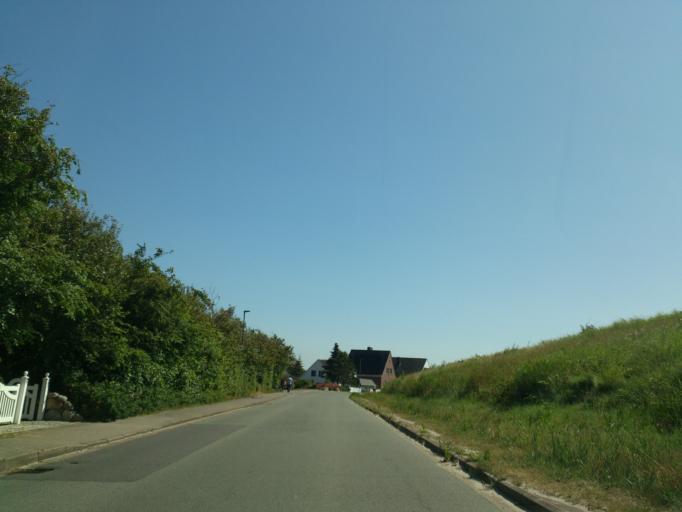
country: DE
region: Schleswig-Holstein
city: Sankt Peter-Ording
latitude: 54.3296
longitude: 8.6073
